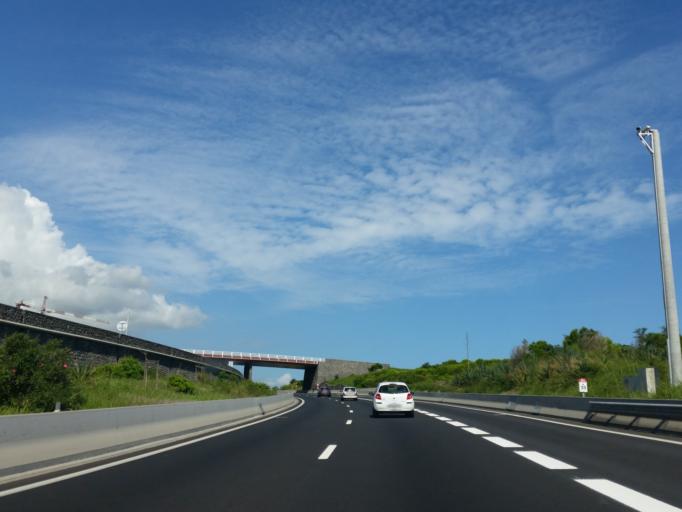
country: RE
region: Reunion
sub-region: Reunion
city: Saint-Paul
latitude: -21.0384
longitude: 55.2482
